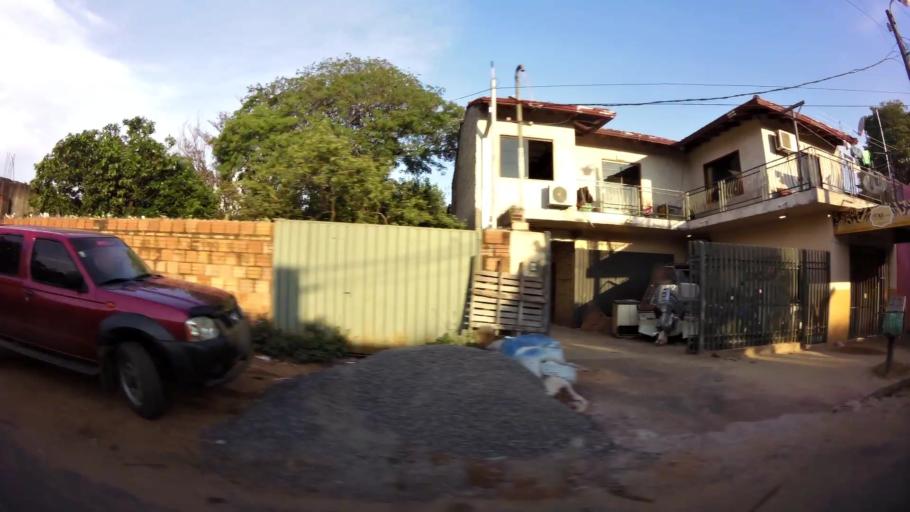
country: PY
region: Central
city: San Lorenzo
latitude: -25.3593
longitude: -57.5057
